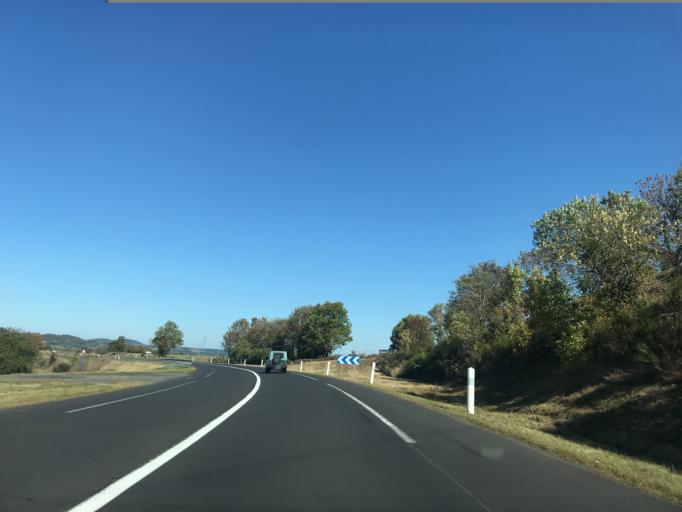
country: FR
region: Auvergne
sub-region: Departement du Puy-de-Dome
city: Gelles
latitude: 45.7070
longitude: 2.8110
